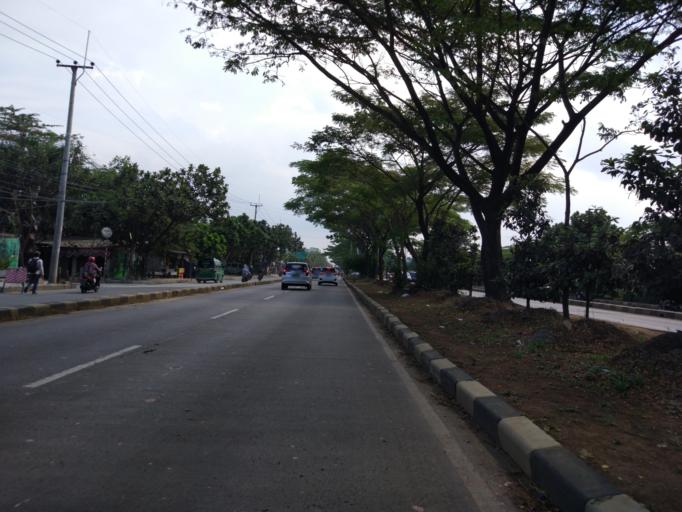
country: ID
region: West Java
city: Cileunyi
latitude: -6.9360
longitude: 107.7083
